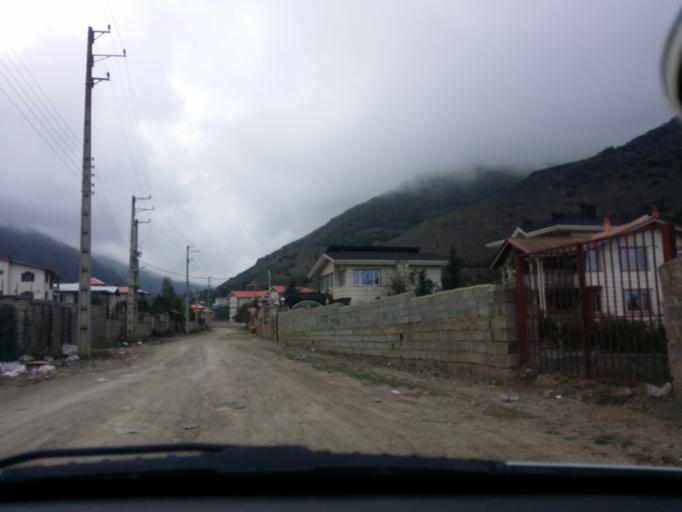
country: IR
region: Mazandaran
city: `Abbasabad
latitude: 36.4874
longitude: 51.1342
